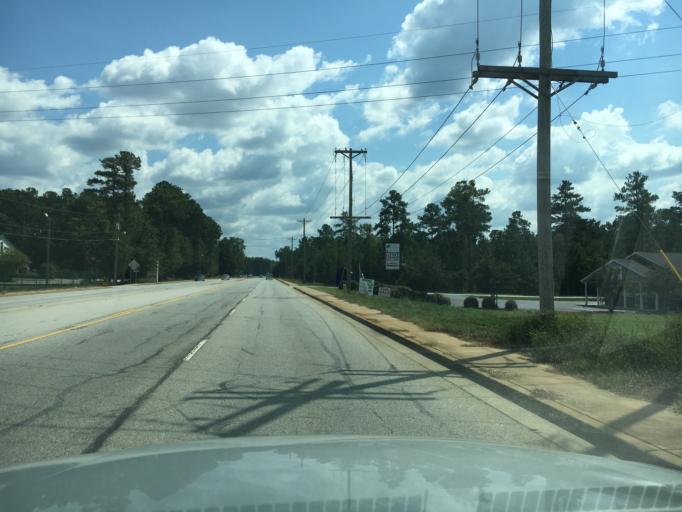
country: US
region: South Carolina
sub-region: Greenwood County
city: Greenwood
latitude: 34.2018
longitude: -82.1981
